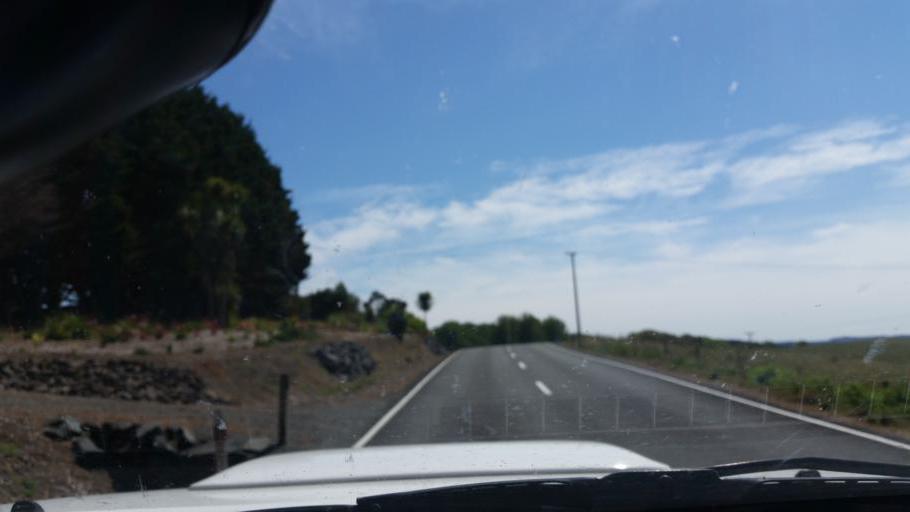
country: NZ
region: Auckland
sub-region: Auckland
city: Wellsford
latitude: -36.2205
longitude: 174.3805
